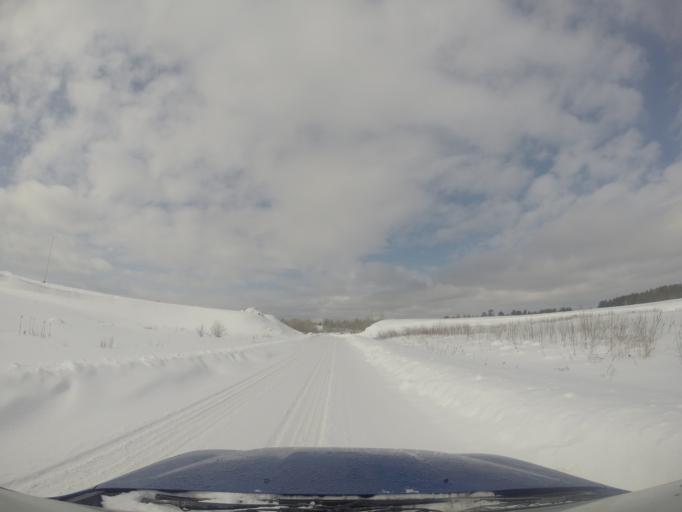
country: CA
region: Ontario
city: Greater Sudbury
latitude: 46.1047
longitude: -80.6687
